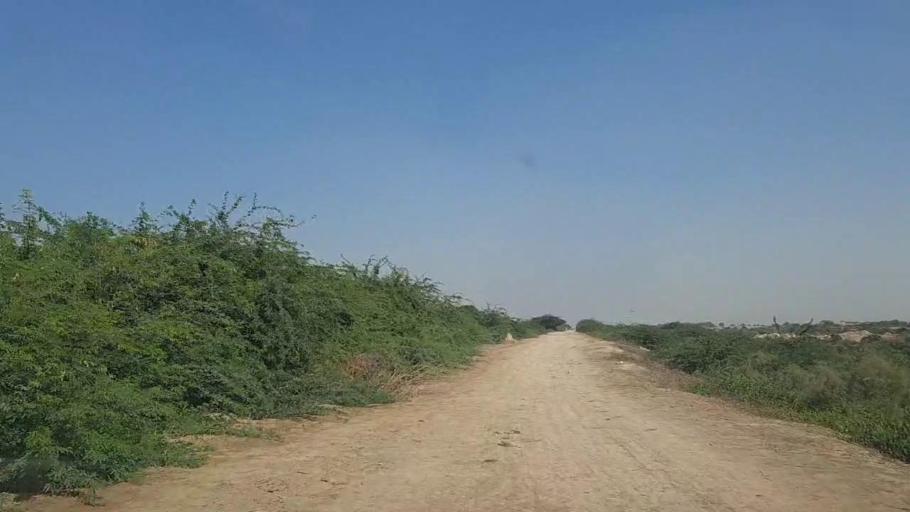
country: PK
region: Sindh
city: Thatta
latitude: 24.8504
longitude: 68.0283
